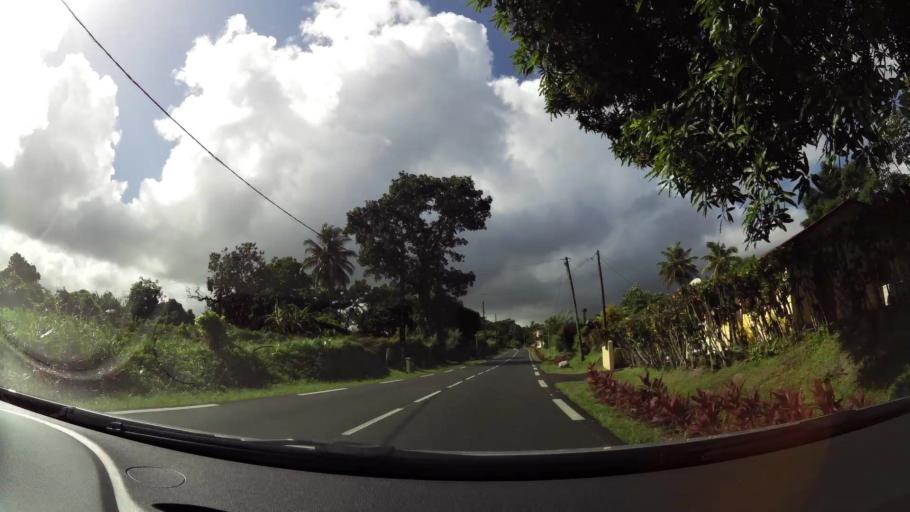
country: MQ
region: Martinique
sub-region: Martinique
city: Basse-Pointe
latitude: 14.8280
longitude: -61.1093
